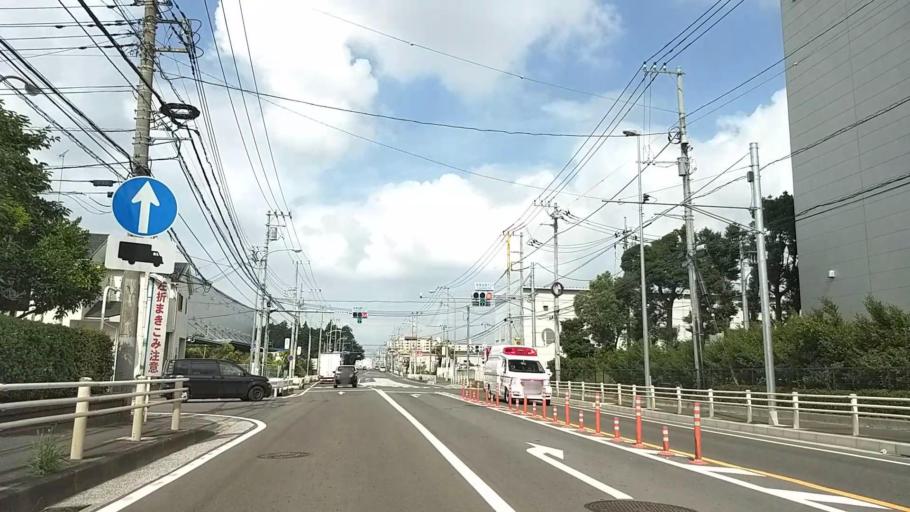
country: JP
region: Kanagawa
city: Minami-rinkan
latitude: 35.4981
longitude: 139.4802
